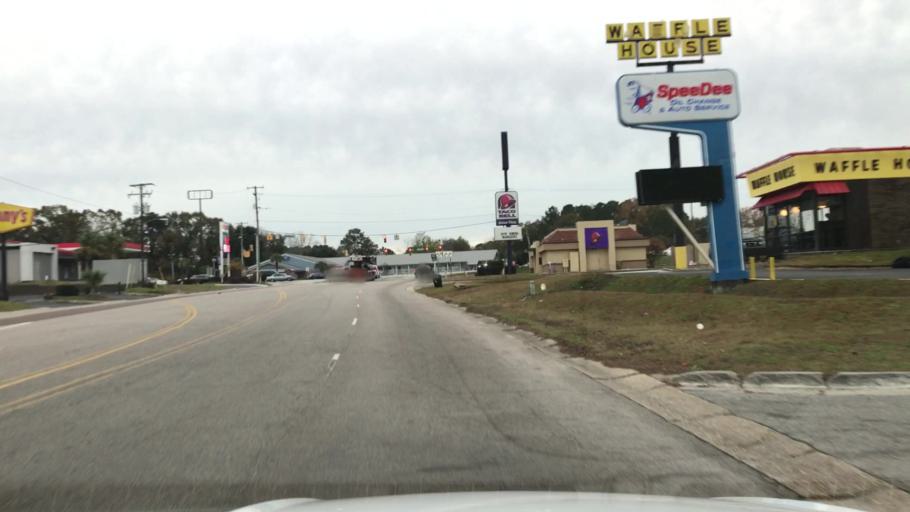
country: US
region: South Carolina
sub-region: Berkeley County
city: Hanahan
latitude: 32.9367
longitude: -80.0456
